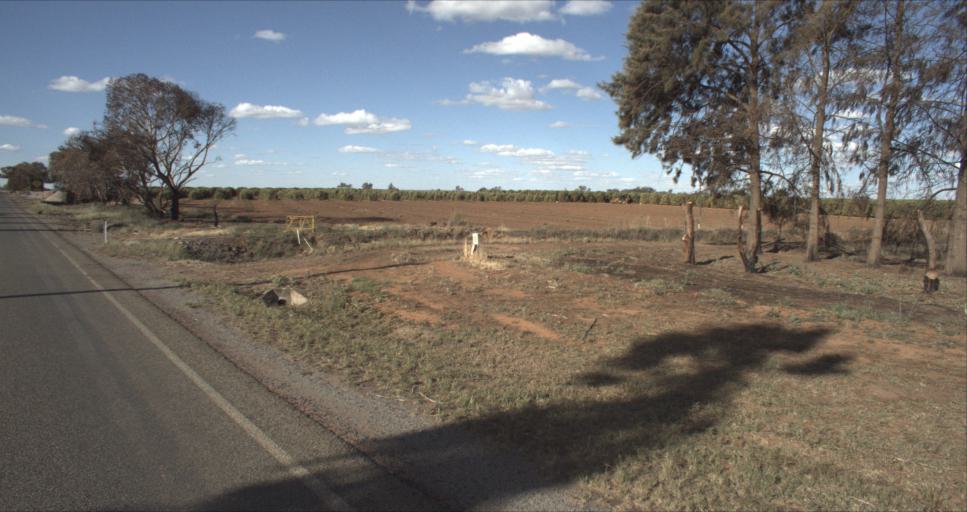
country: AU
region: New South Wales
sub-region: Leeton
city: Leeton
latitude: -34.5235
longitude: 146.2828
